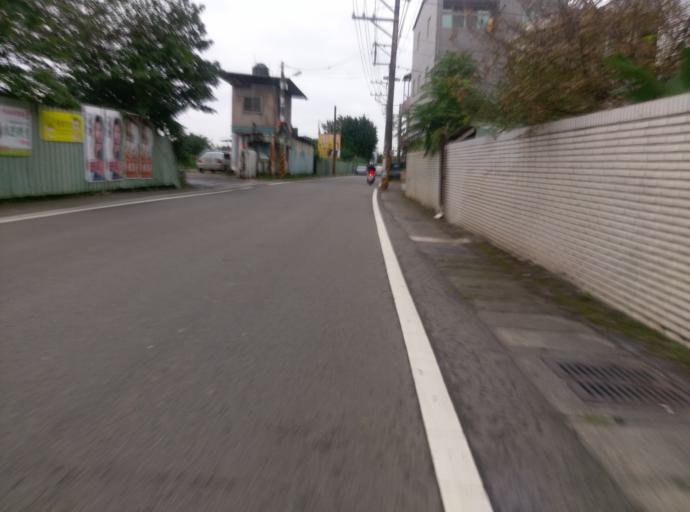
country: TW
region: Taiwan
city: Daxi
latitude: 24.9145
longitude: 121.2383
